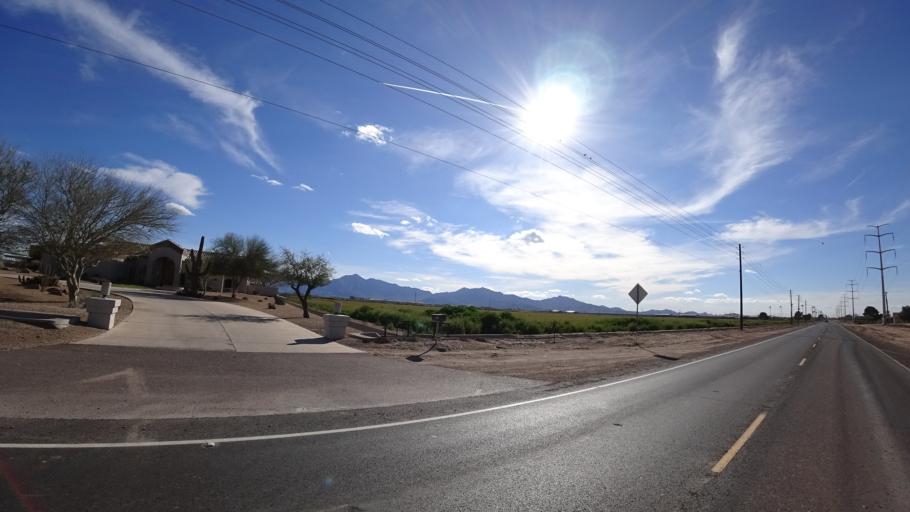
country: US
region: Arizona
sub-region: Maricopa County
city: Tolleson
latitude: 33.4081
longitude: -112.2404
